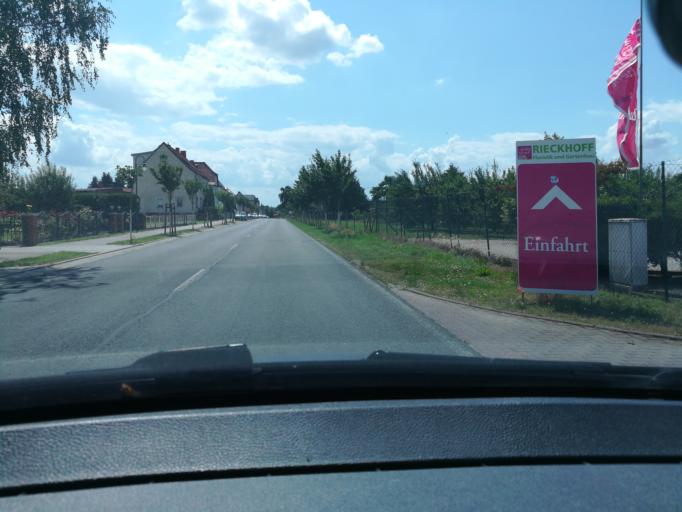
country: DE
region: Saxony-Anhalt
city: Rogatz
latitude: 52.3225
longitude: 11.7711
